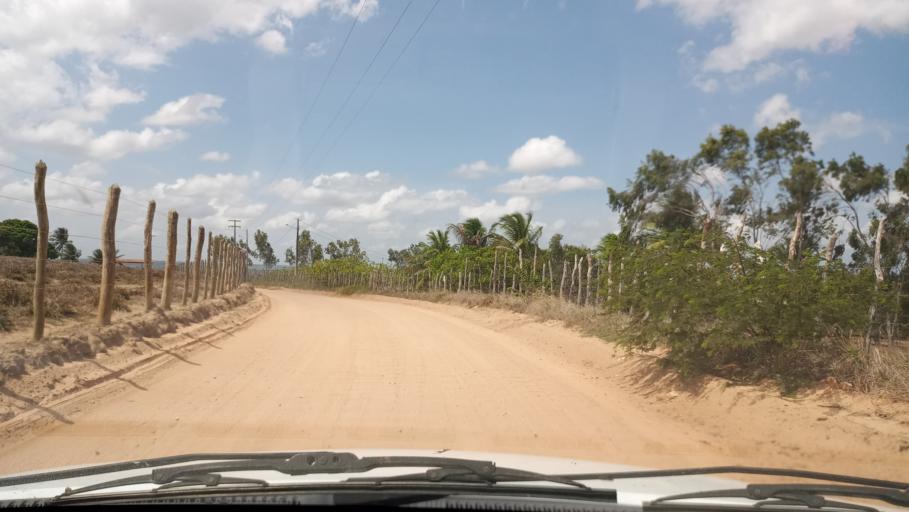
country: BR
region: Rio Grande do Norte
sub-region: Goianinha
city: Goianinha
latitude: -6.3414
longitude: -35.3262
